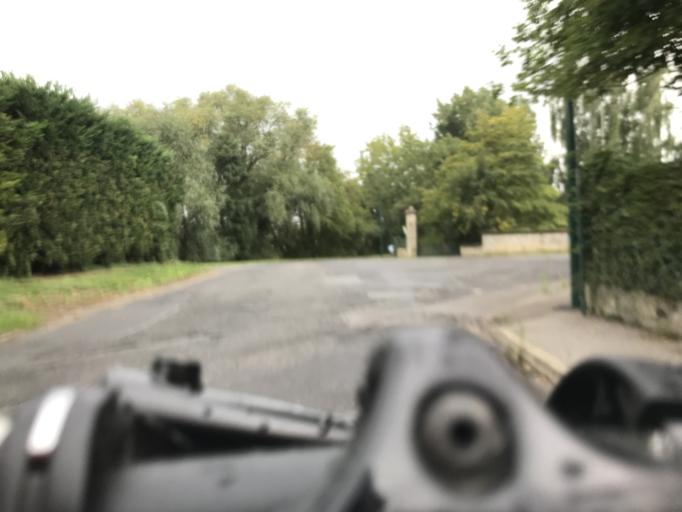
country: FR
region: Picardie
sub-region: Departement de l'Oise
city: Saint-Maximin
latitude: 49.2193
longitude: 2.4279
